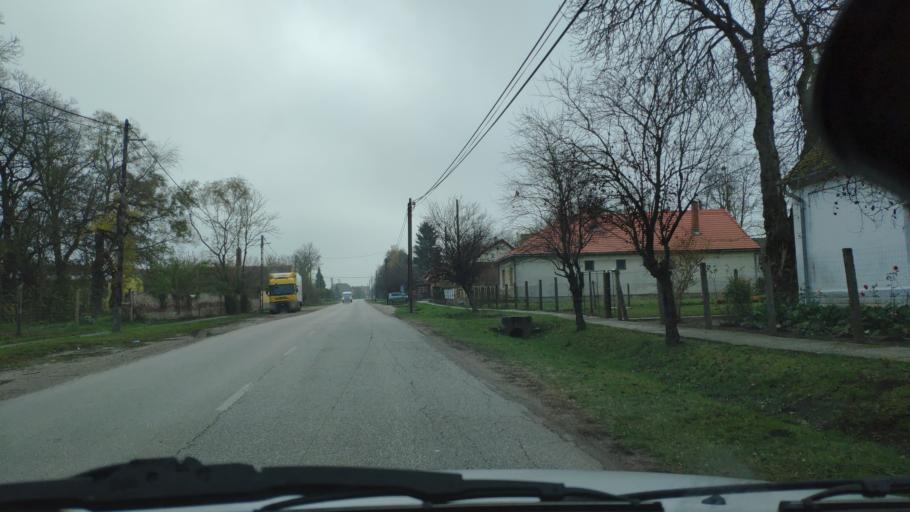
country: HU
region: Somogy
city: Balatonbereny
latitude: 46.6744
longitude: 17.2889
